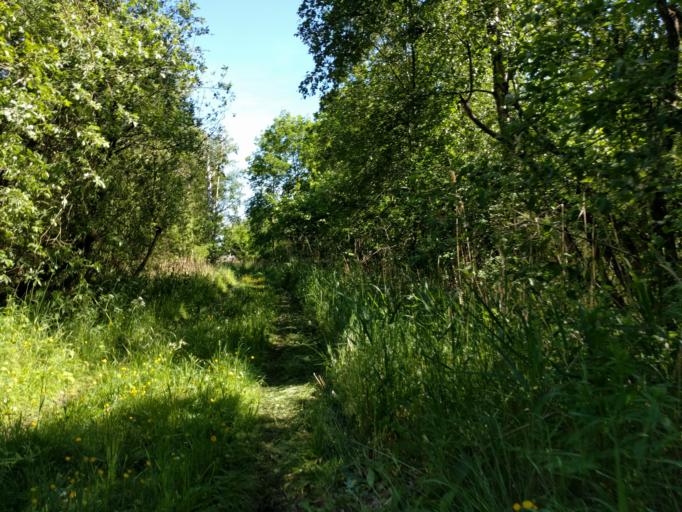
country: DK
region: South Denmark
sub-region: Kerteminde Kommune
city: Langeskov
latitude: 55.3825
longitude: 10.5915
